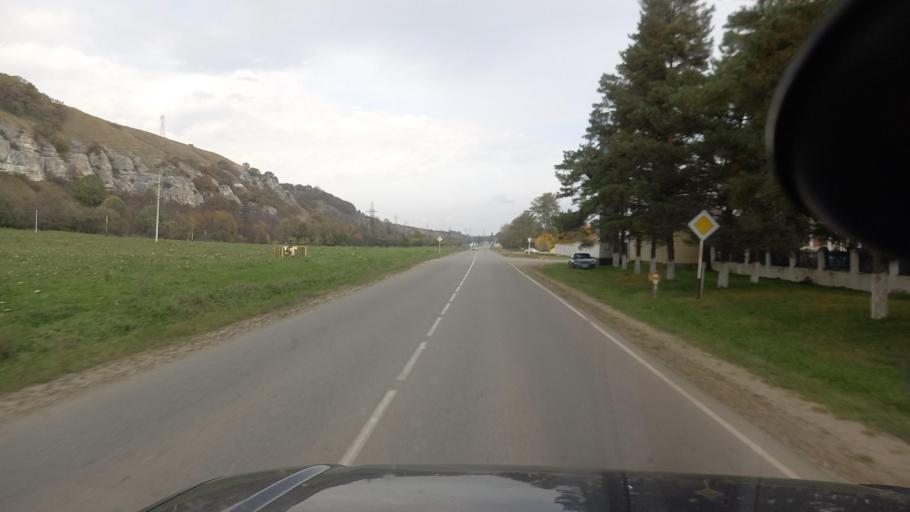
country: RU
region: Krasnodarskiy
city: Psebay
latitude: 44.1500
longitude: 40.8295
